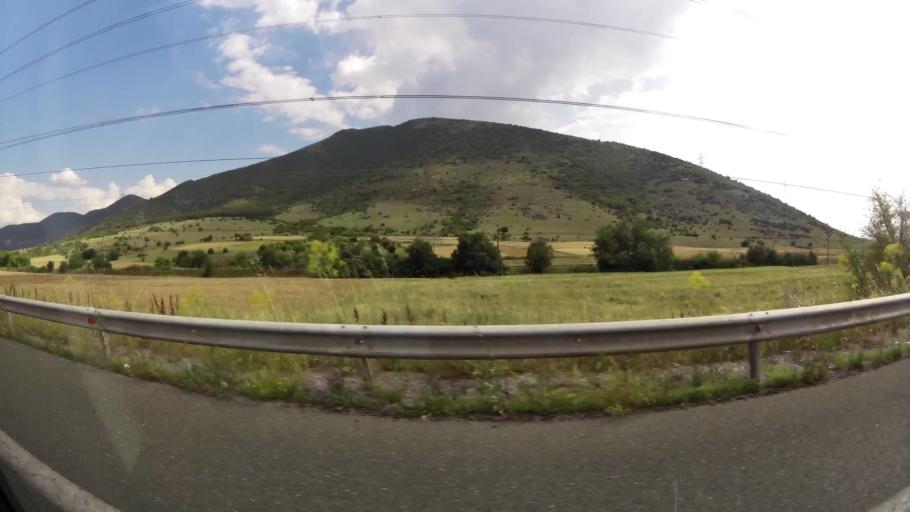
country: GR
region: West Macedonia
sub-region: Nomos Kozanis
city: Akrini
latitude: 40.3694
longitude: 21.8933
